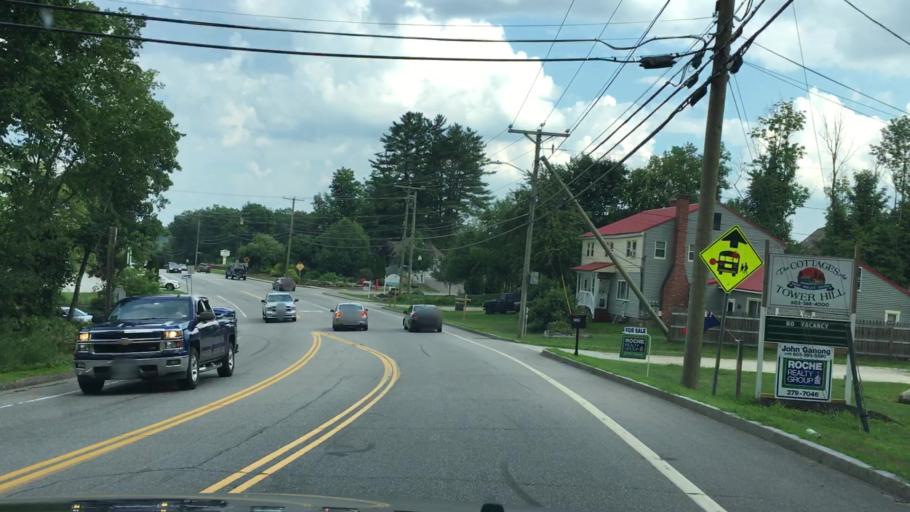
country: US
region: New Hampshire
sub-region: Belknap County
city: Meredith
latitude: 43.6061
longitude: -71.4653
